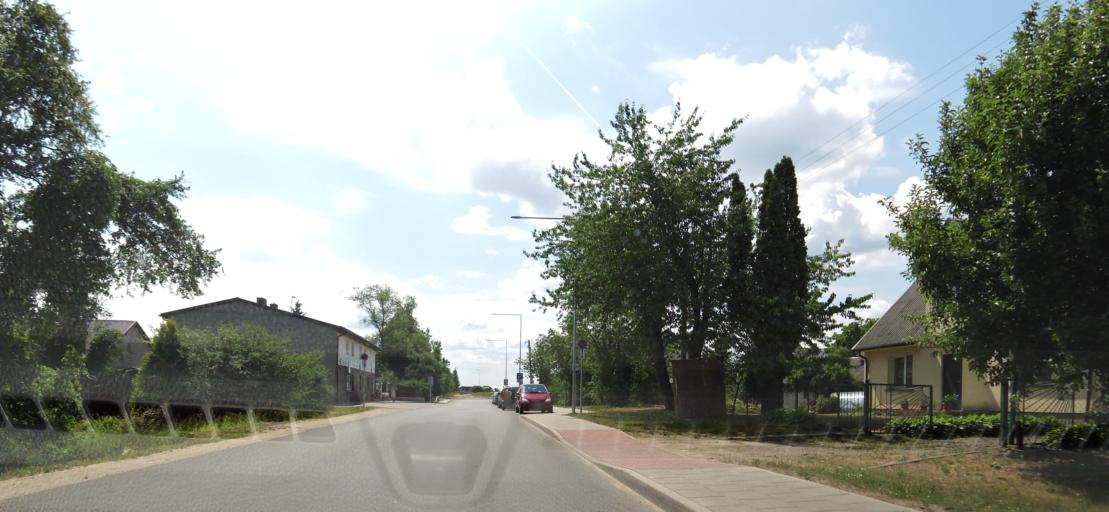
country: LT
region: Vilnius County
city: Pasilaiciai
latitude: 54.7599
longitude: 25.2077
